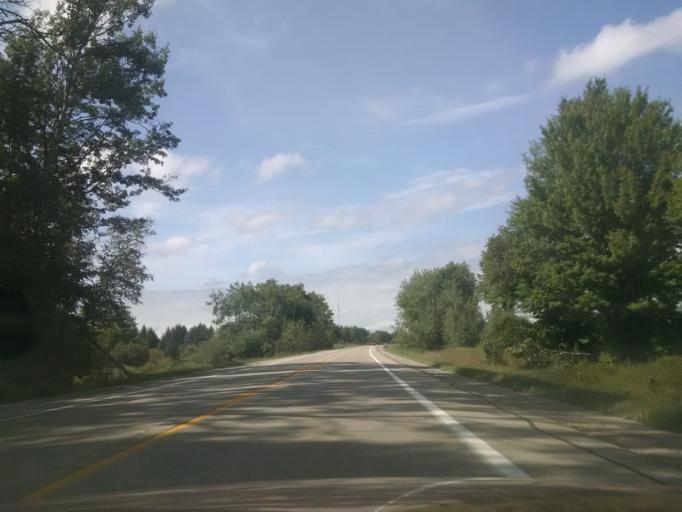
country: US
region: Michigan
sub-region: Clare County
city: Clare
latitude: 43.8805
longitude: -84.9536
